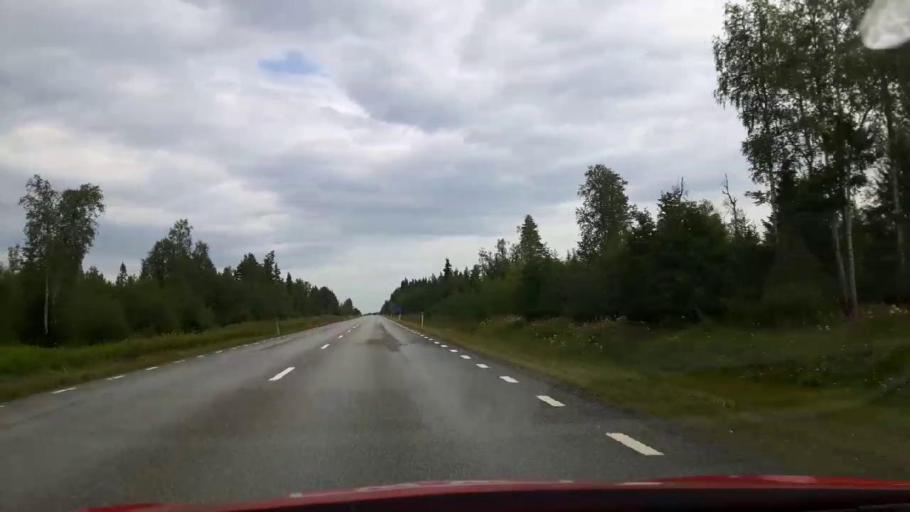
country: SE
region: Jaemtland
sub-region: Stroemsunds Kommun
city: Stroemsund
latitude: 63.6957
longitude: 15.4304
